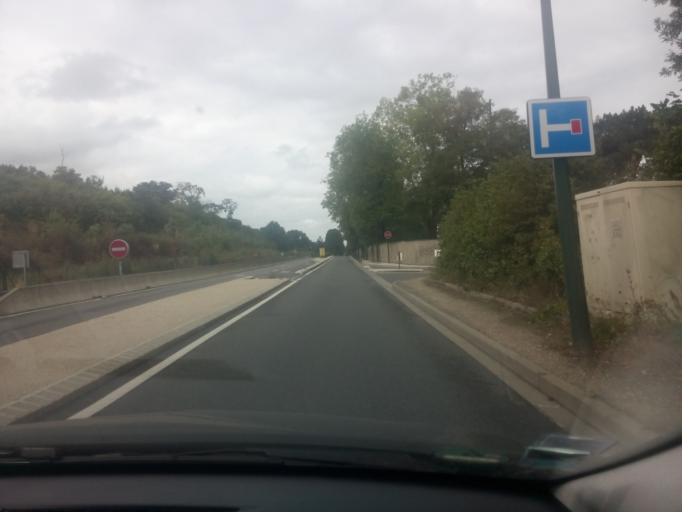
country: FR
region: Ile-de-France
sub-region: Departement de l'Essonne
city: Bievres
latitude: 48.7494
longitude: 2.2145
